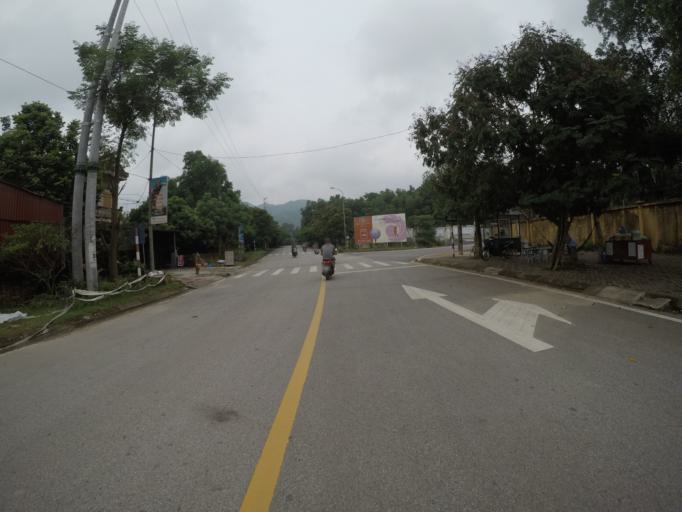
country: VN
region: Ha Noi
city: Soc Son
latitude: 21.2838
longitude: 105.8401
